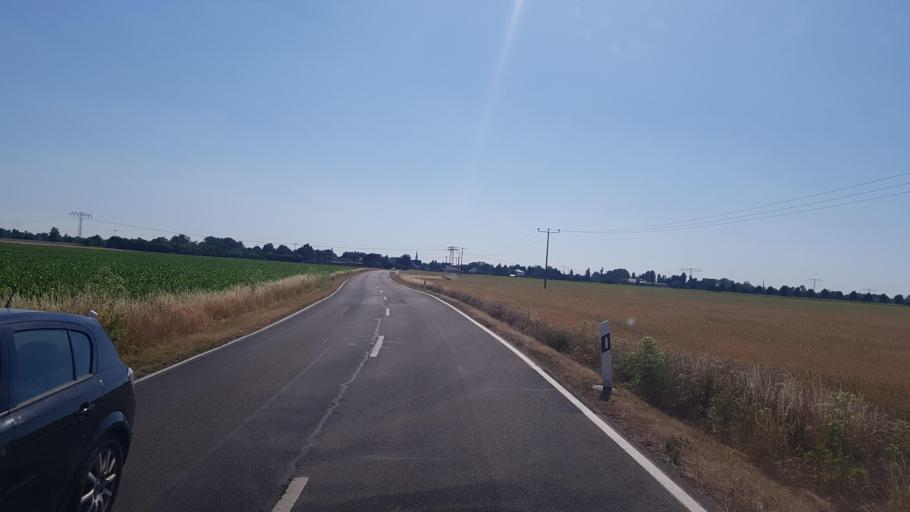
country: DE
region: Saxony-Anhalt
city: Prettin
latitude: 51.6690
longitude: 12.9498
